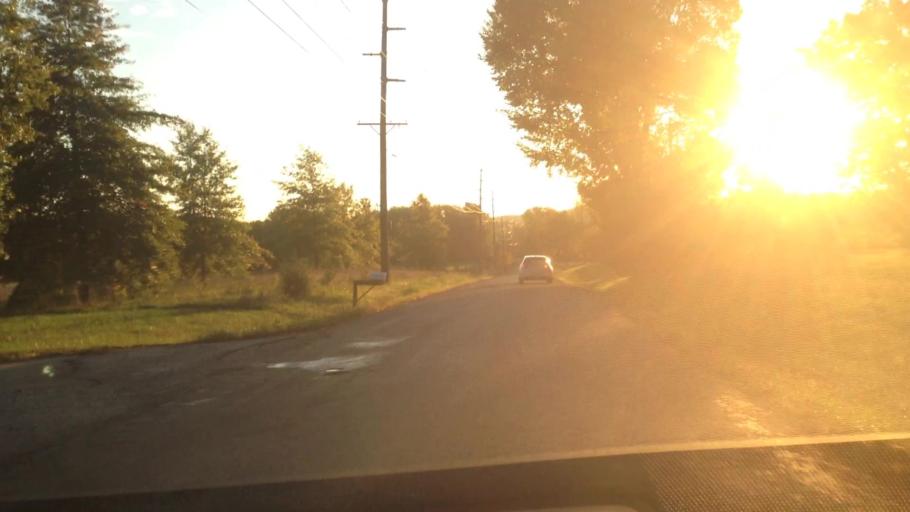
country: US
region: Kansas
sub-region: Johnson County
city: De Soto
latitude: 38.9567
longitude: -94.9919
